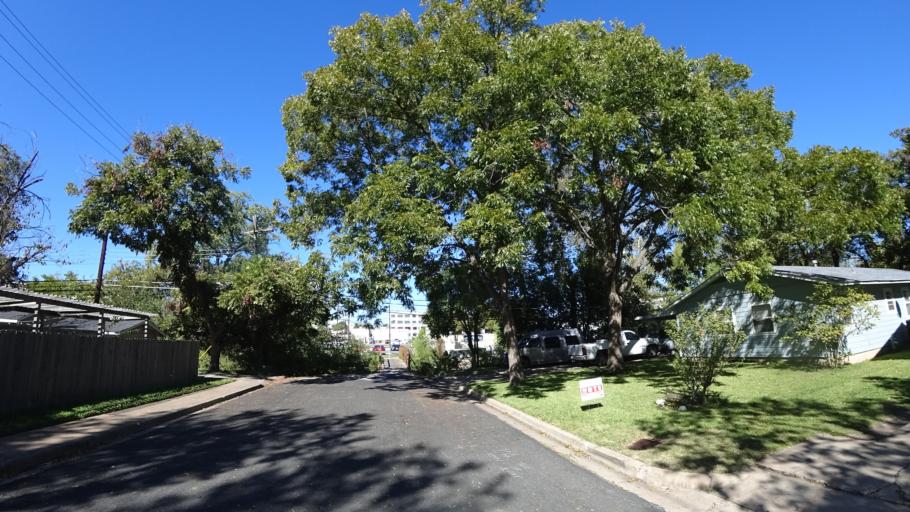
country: US
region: Texas
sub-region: Travis County
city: Austin
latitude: 30.3258
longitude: -97.7205
